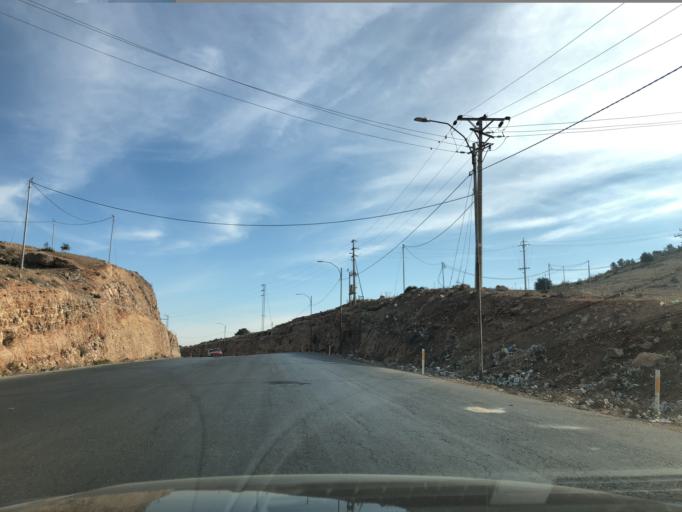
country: JO
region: Irbid
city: `Anjarah
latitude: 32.3043
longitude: 35.7753
